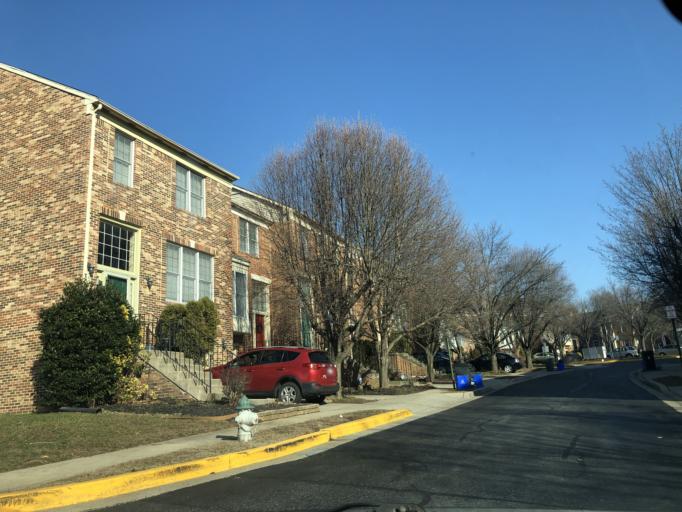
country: US
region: Maryland
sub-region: Montgomery County
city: Burtonsville
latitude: 39.1017
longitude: -76.9325
